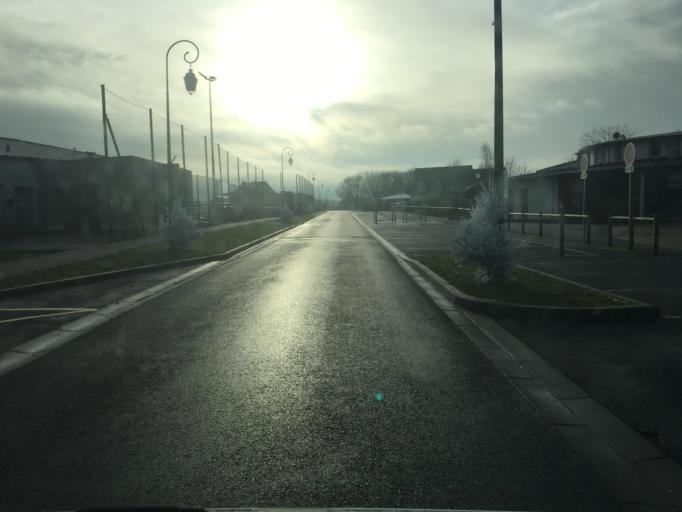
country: FR
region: Lower Normandy
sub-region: Departement du Calvados
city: Rots
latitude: 49.2054
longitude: -0.4769
